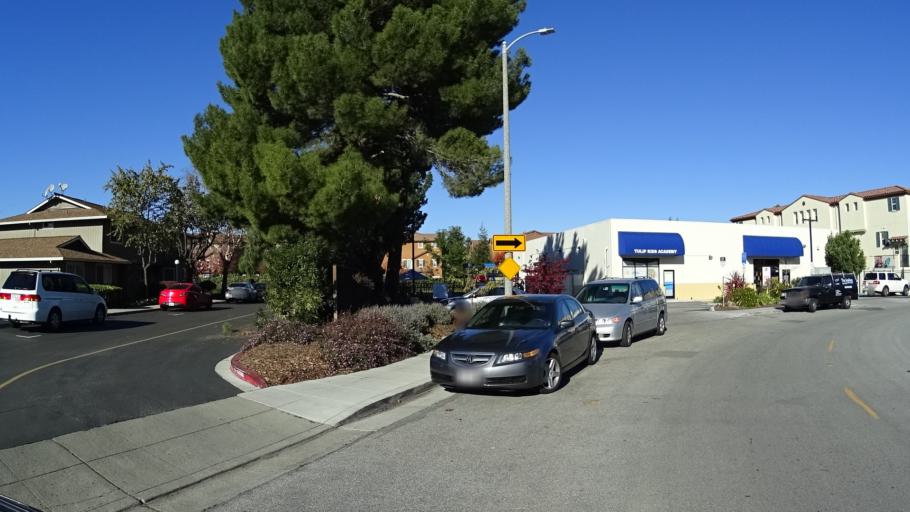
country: US
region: California
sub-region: Santa Clara County
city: Sunnyvale
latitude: 37.3680
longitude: -121.9982
